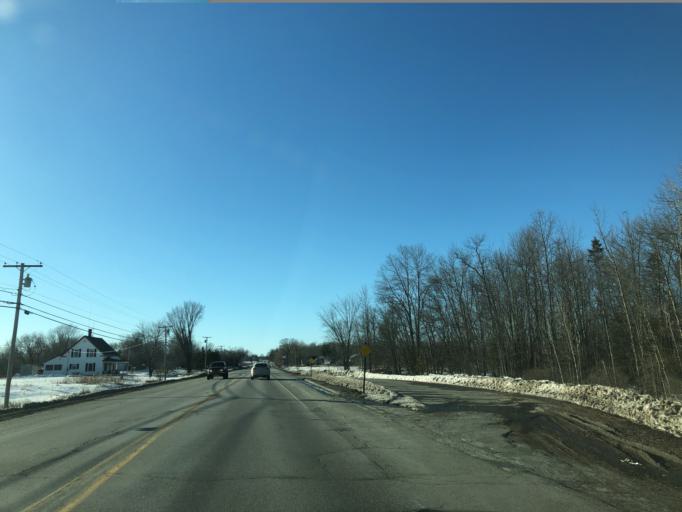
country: US
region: Maine
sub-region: Penobscot County
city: Kenduskeag
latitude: 44.9838
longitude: -69.0032
